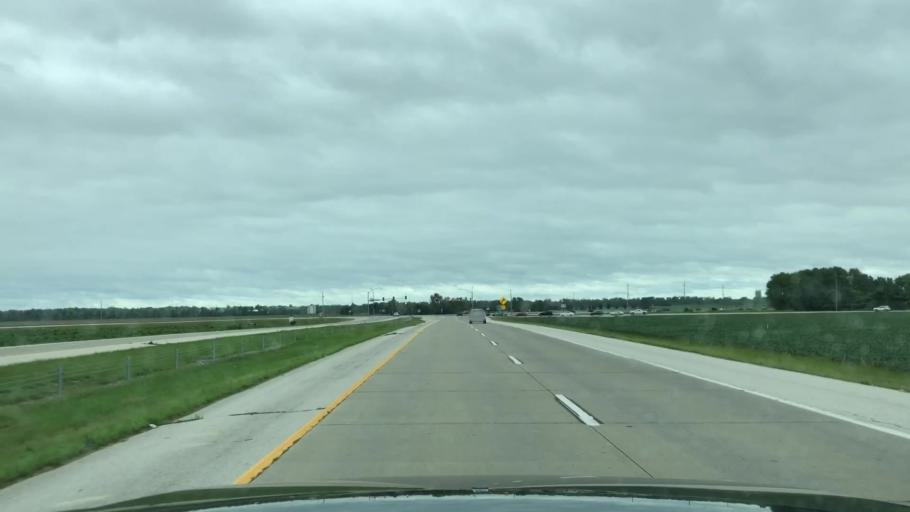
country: US
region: Missouri
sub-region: Saint Charles County
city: Saint Charles
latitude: 38.7222
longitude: -90.4981
